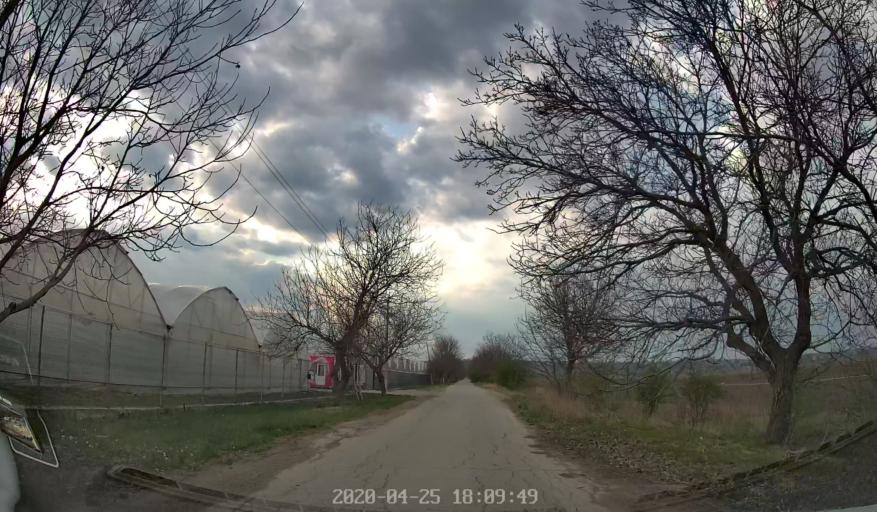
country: MD
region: Chisinau
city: Vadul lui Voda
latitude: 47.1312
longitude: 29.0796
